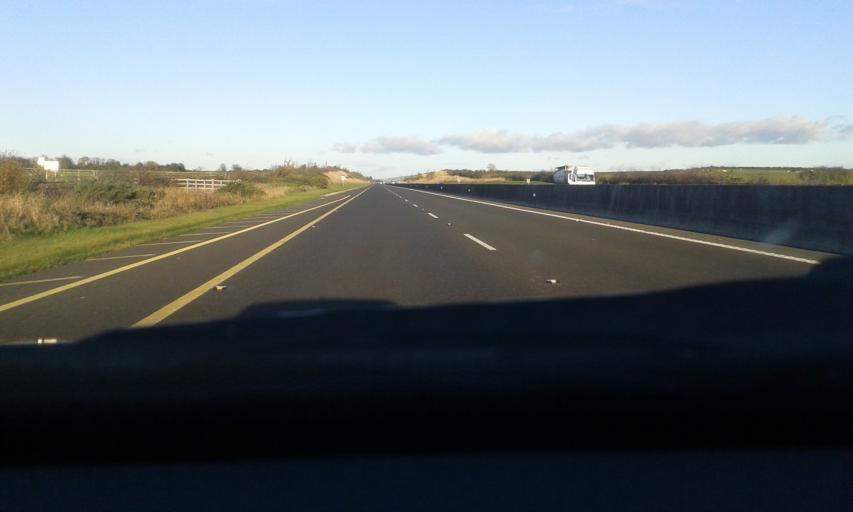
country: IE
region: Munster
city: Thurles
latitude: 52.6961
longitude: -7.6556
